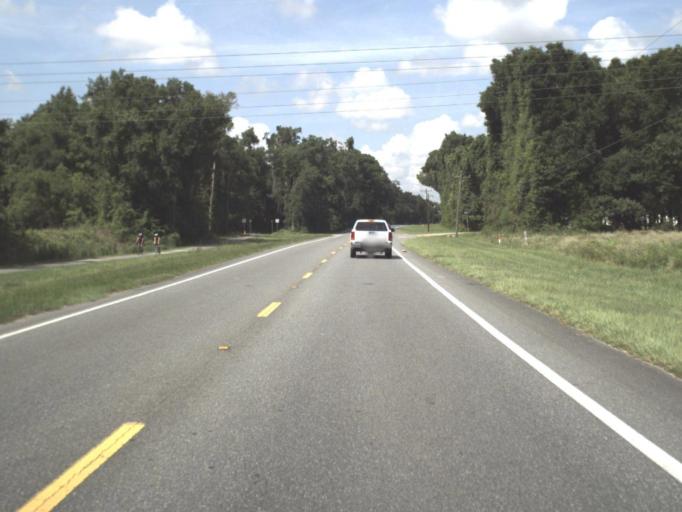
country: US
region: Florida
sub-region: Alachua County
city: Archer
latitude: 29.5496
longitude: -82.4982
